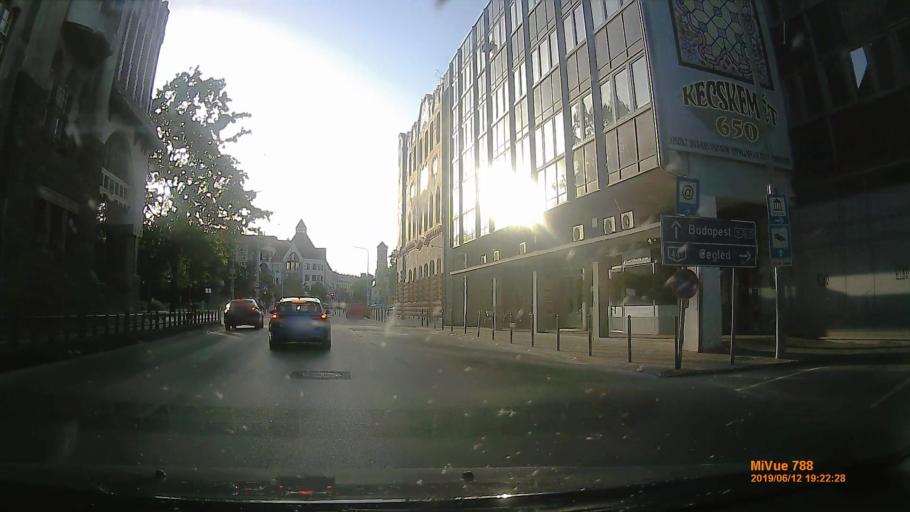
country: HU
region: Bacs-Kiskun
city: Kecskemet
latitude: 46.9081
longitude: 19.6952
